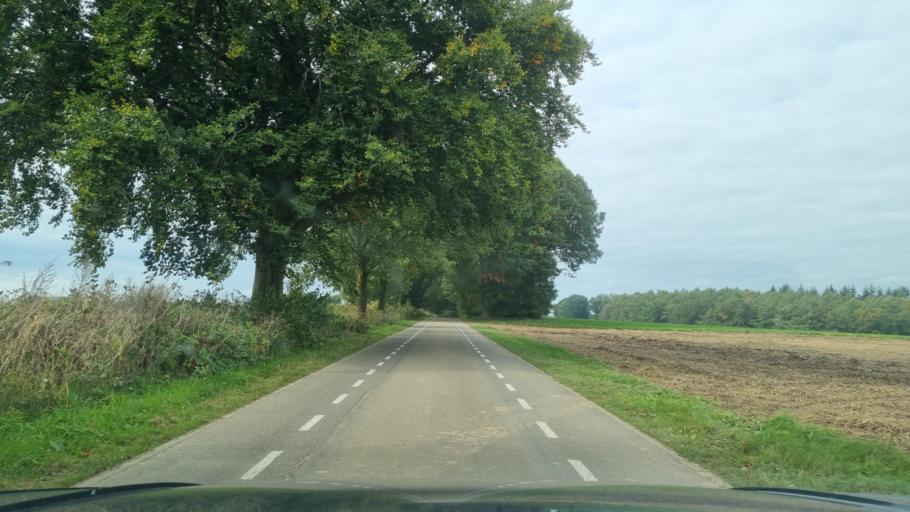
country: NL
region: Gelderland
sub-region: Gemeente Groesbeek
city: Groesbeek
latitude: 51.7957
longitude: 5.9419
